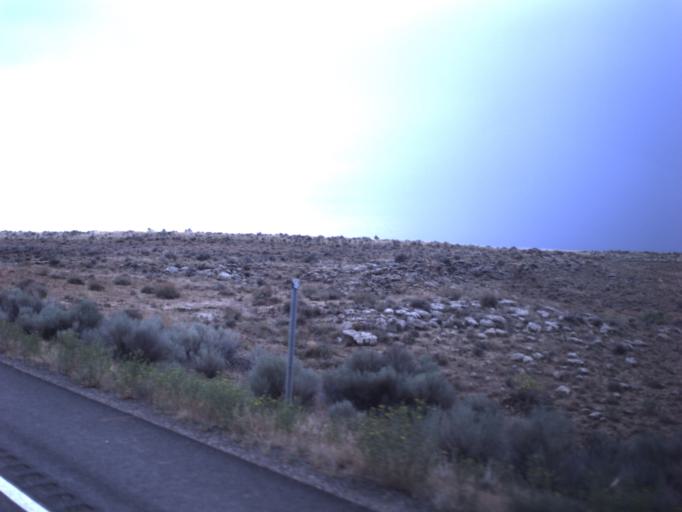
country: US
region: Utah
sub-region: Uintah County
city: Naples
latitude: 40.2935
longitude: -109.4766
